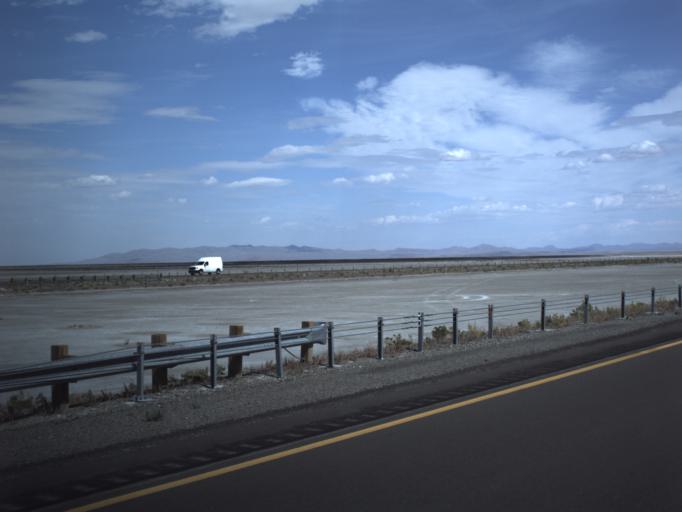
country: US
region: Utah
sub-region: Tooele County
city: Wendover
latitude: 40.7279
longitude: -113.3586
